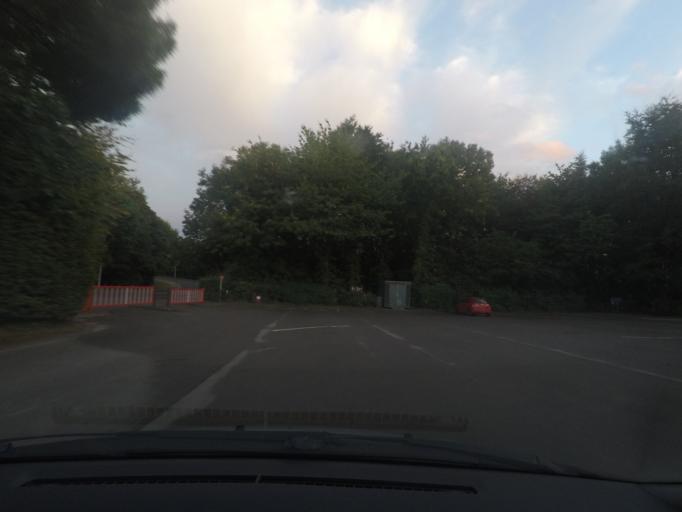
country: GB
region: England
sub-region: East Riding of Yorkshire
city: Hessle
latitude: 53.7191
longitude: -0.4531
